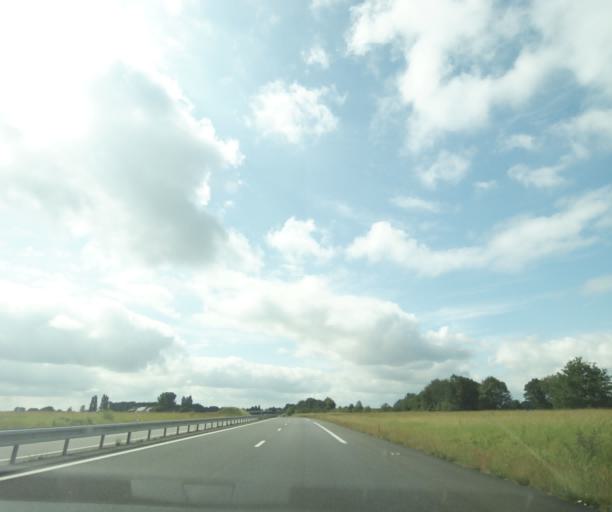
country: FR
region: Pays de la Loire
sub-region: Departement de Maine-et-Loire
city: Vivy
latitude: 47.3628
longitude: -0.0828
